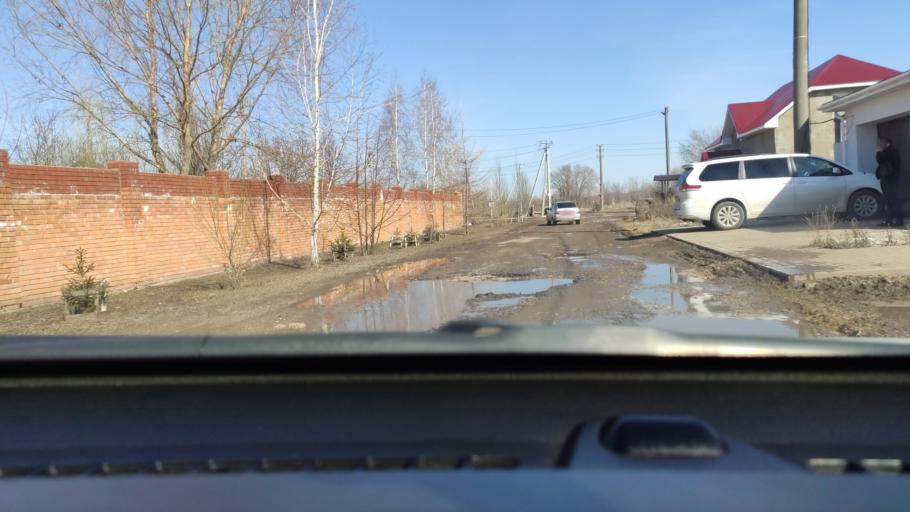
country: RU
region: Samara
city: Podstepki
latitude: 53.5121
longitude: 49.1914
